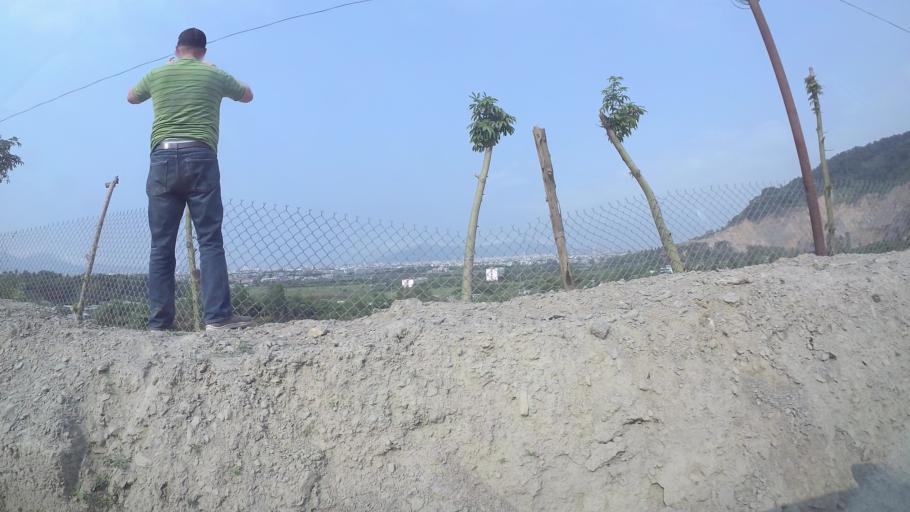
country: VN
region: Da Nang
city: Lien Chieu
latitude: 16.0392
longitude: 108.1523
